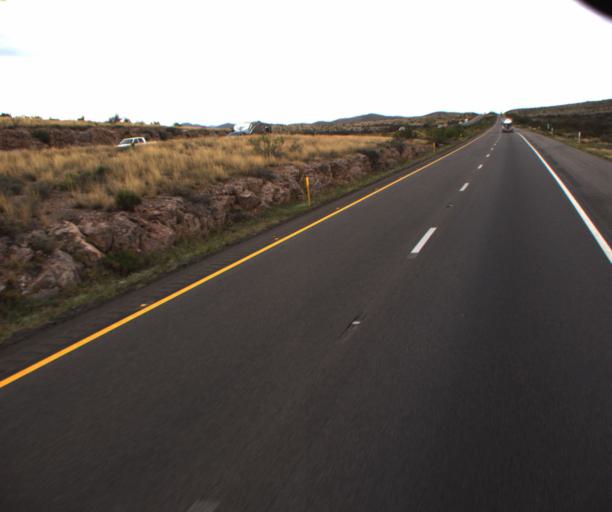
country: US
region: Arizona
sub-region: Cochise County
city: Willcox
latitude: 32.1457
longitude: -109.9976
